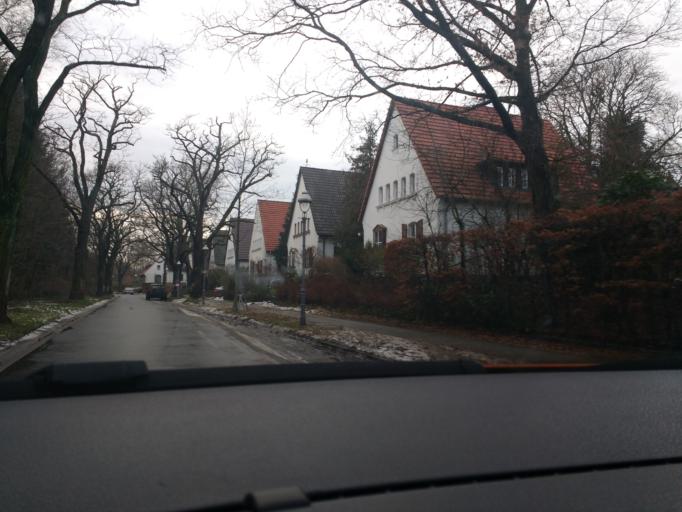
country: DE
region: Berlin
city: Zehlendorf Bezirk
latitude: 52.4344
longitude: 13.2414
